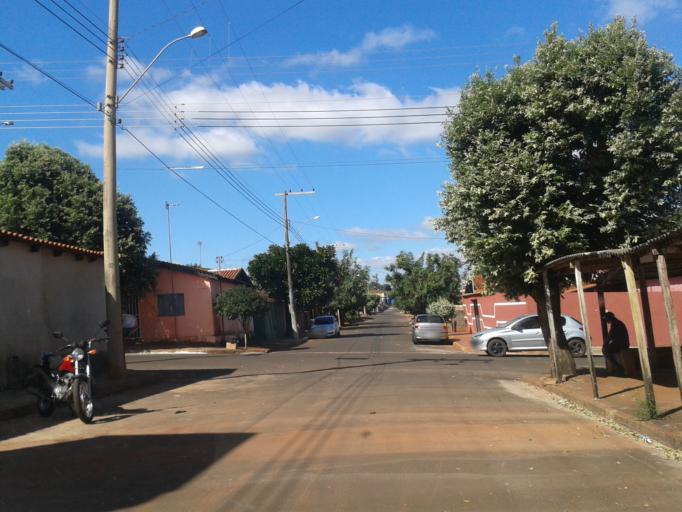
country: BR
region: Minas Gerais
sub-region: Centralina
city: Centralina
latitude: -18.5813
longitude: -49.1961
